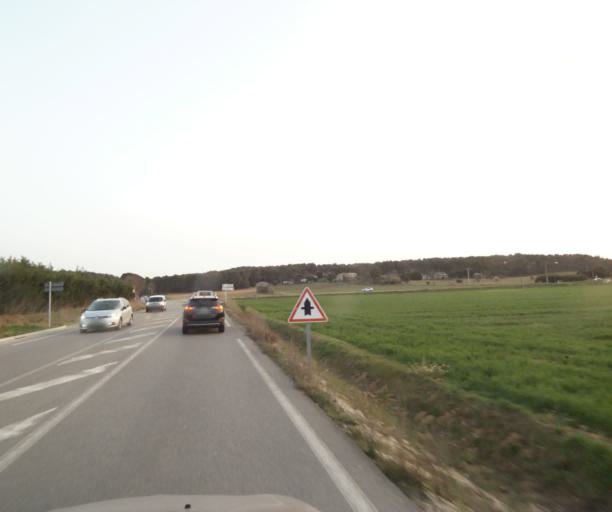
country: FR
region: Provence-Alpes-Cote d'Azur
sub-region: Departement des Bouches-du-Rhone
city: Cabries
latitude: 43.4415
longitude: 5.3613
